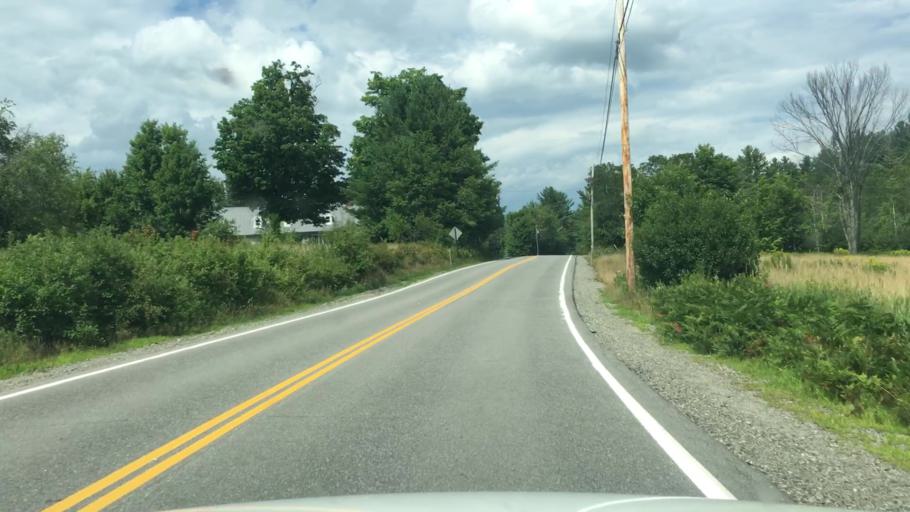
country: US
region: New Hampshire
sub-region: Coos County
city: Whitefield
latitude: 44.3089
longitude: -71.6589
